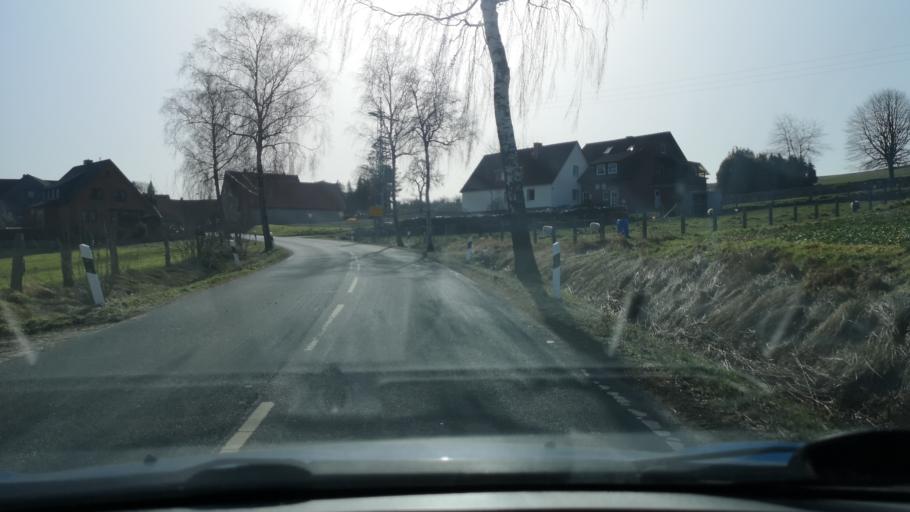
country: DE
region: Lower Saxony
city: Weenzen
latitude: 51.9930
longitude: 9.6489
